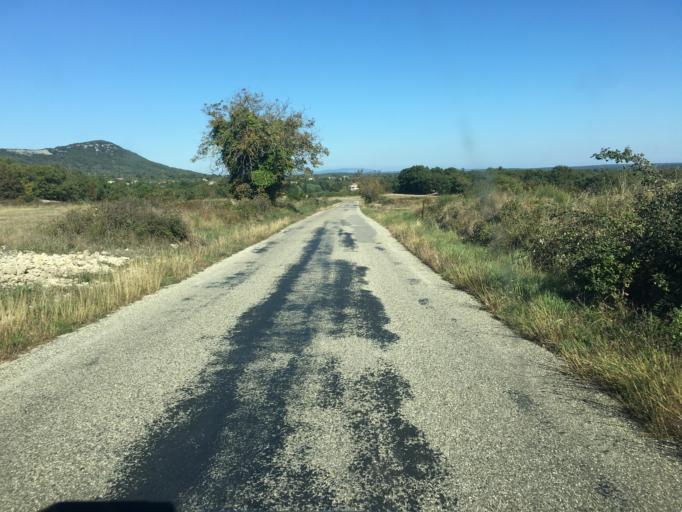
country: FR
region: Languedoc-Roussillon
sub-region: Departement du Gard
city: Barjac
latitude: 44.1774
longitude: 4.3249
